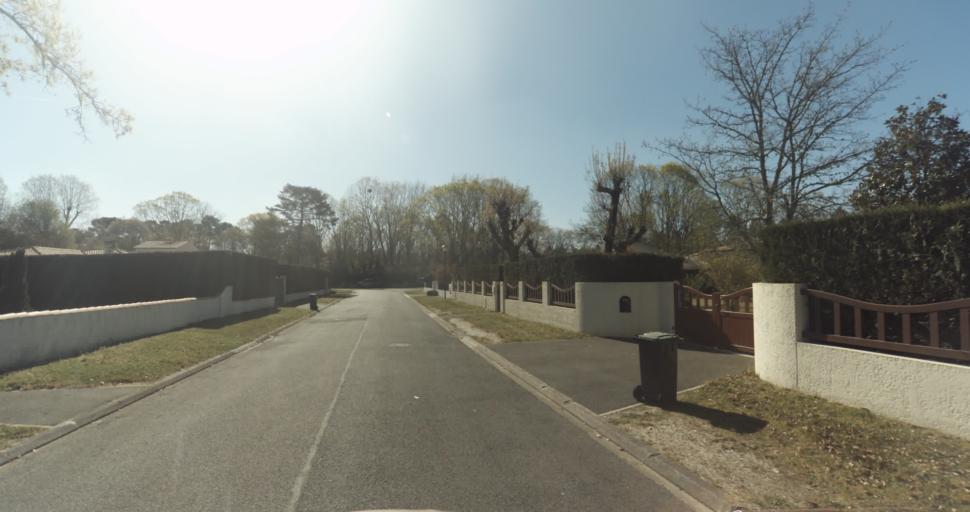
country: FR
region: Aquitaine
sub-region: Departement de la Gironde
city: Martignas-sur-Jalle
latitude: 44.7947
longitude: -0.8405
